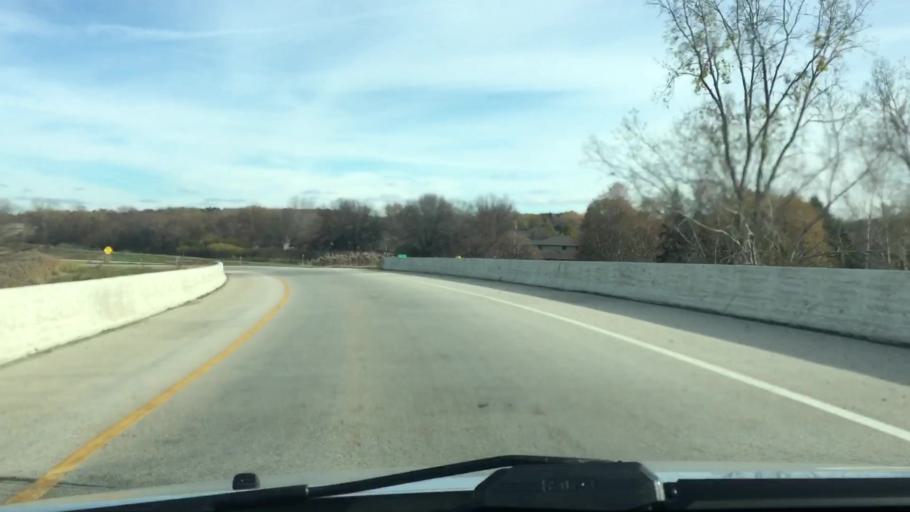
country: US
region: Wisconsin
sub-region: Brown County
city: Green Bay
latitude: 44.5167
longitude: -87.9579
